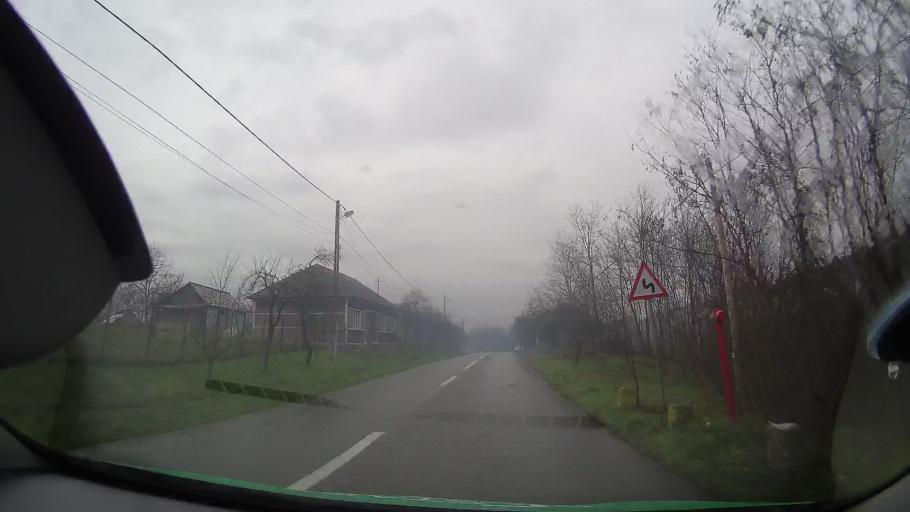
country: RO
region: Bihor
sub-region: Comuna Holod
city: Vintere
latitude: 46.7691
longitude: 22.1402
